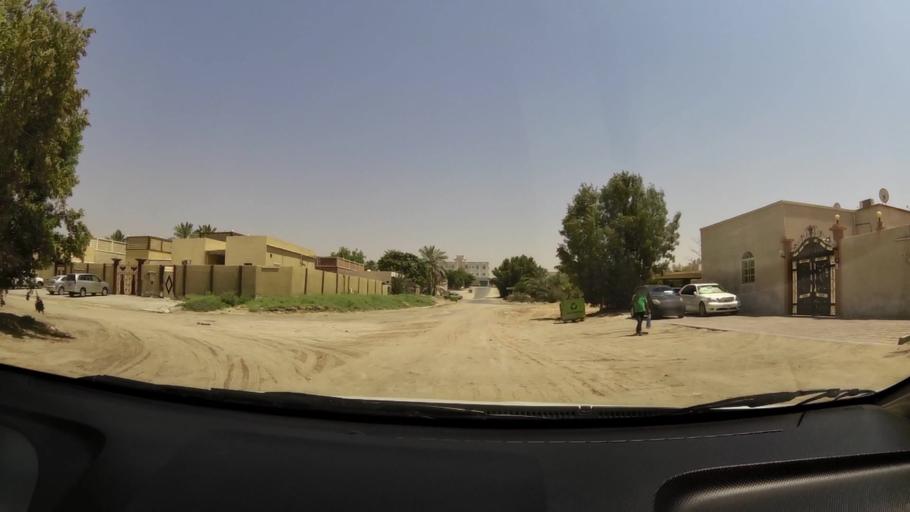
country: AE
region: Umm al Qaywayn
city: Umm al Qaywayn
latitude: 25.5035
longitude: 55.5752
